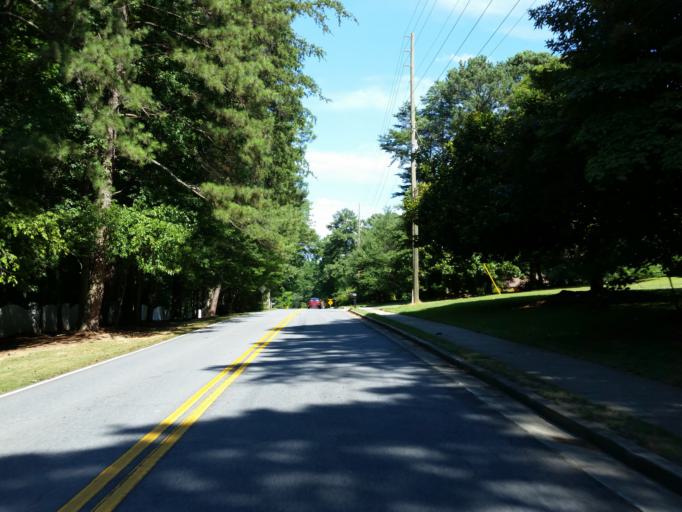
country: US
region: Georgia
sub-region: Cobb County
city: Marietta
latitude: 33.9691
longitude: -84.4701
